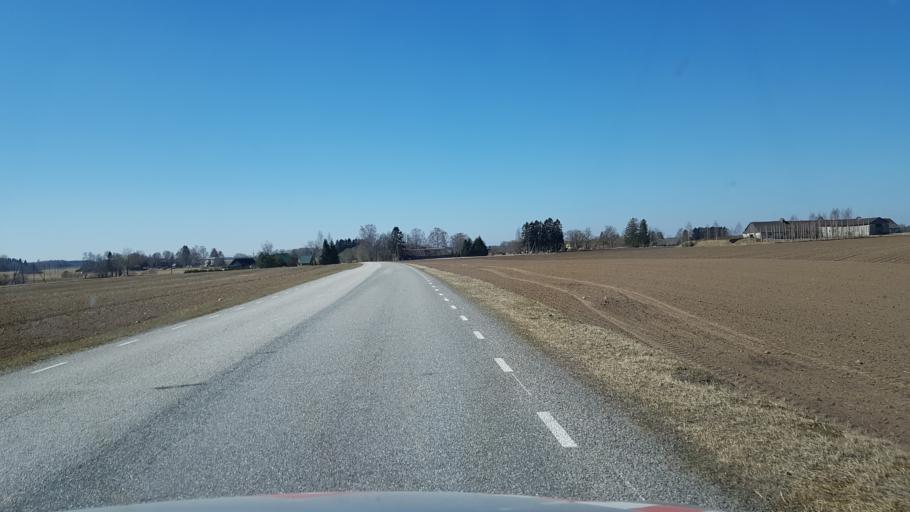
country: EE
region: Laeaene-Virumaa
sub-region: Vinni vald
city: Vinni
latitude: 59.0680
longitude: 26.4951
